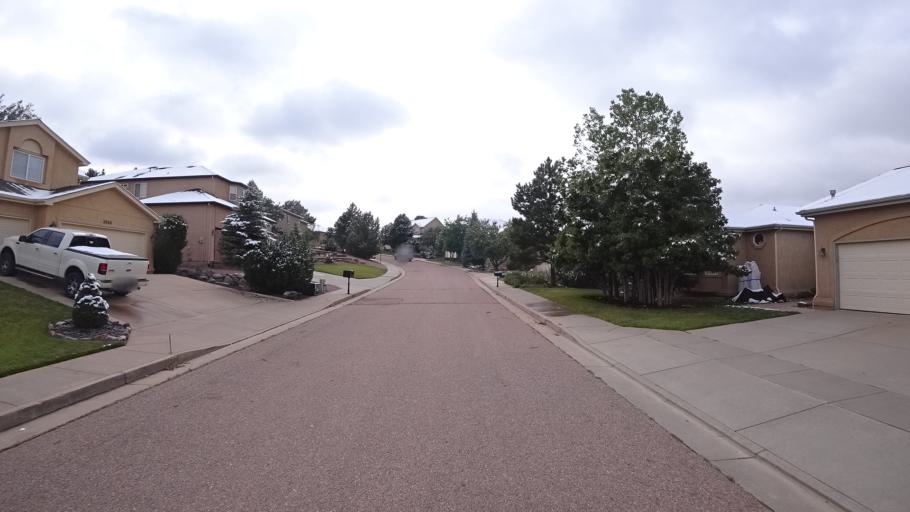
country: US
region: Colorado
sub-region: El Paso County
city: Colorado Springs
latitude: 38.9143
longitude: -104.7963
